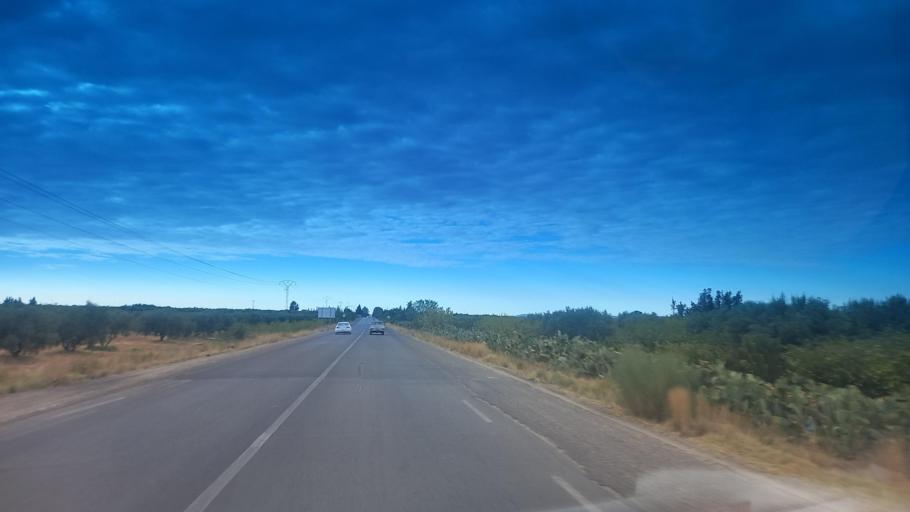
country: TN
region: Al Qasrayn
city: Sbiba
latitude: 35.3077
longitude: 9.0866
